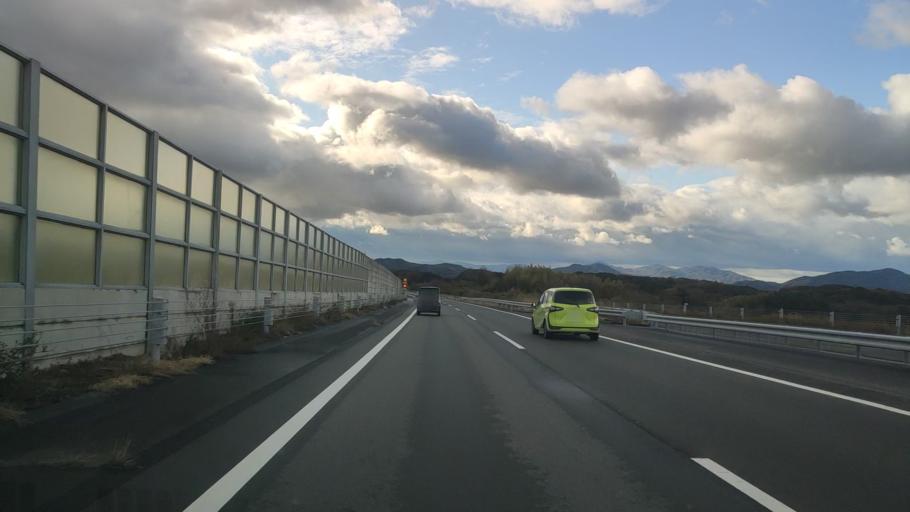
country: JP
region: Hyogo
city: Sumoto
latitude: 34.4681
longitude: 134.8762
